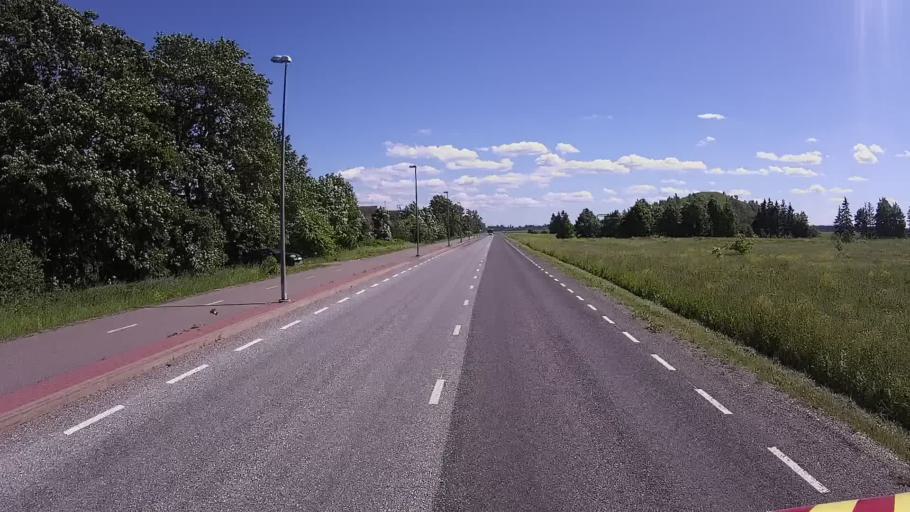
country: EE
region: Ida-Virumaa
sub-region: Kohtla-Jaerve linn
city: Kohtla-Jarve
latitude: 59.3992
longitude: 27.3397
